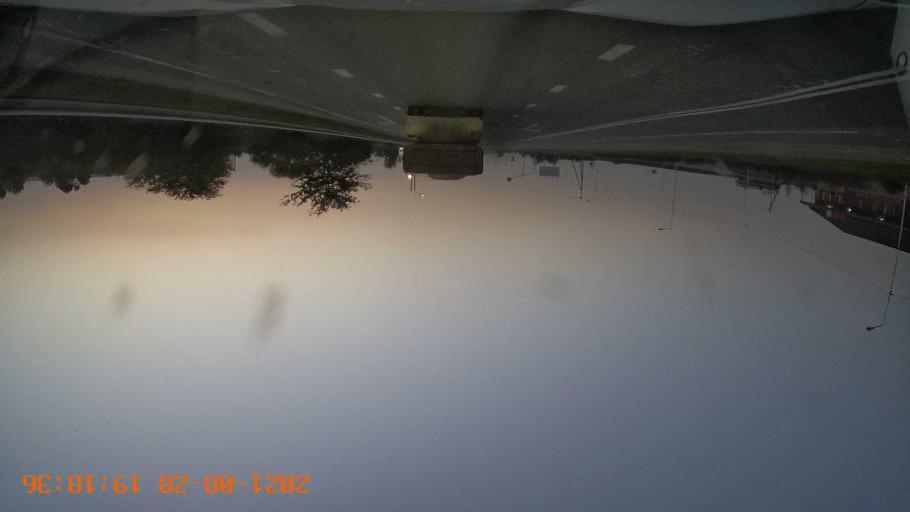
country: RU
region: Krasnodarskiy
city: Ryazanskaya
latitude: 44.8931
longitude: 39.5246
